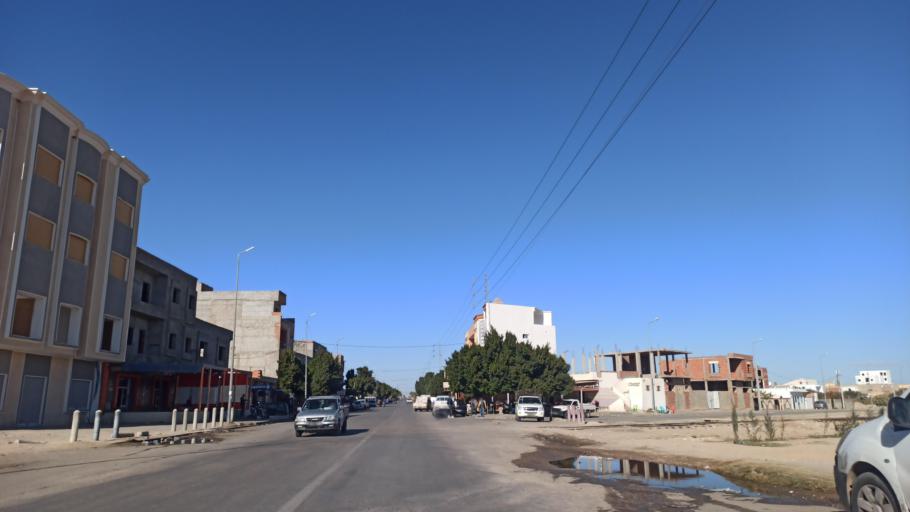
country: TN
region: Sidi Bu Zayd
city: Jilma
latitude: 35.2721
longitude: 9.4190
